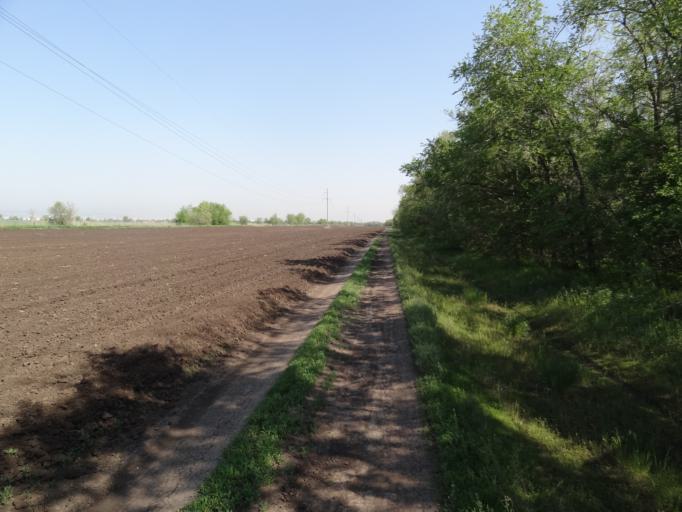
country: RU
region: Saratov
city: Privolzhskiy
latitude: 51.4232
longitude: 46.1074
